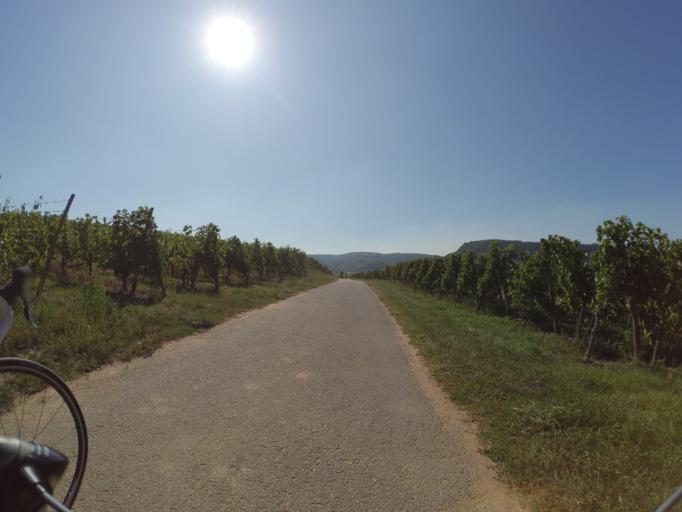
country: DE
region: Rheinland-Pfalz
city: Klusserath
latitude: 49.8384
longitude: 6.8613
